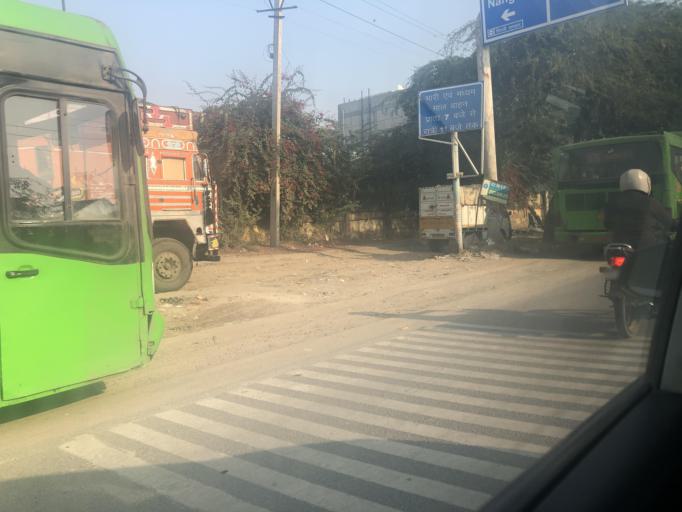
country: IN
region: Haryana
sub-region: Jhajjar
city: Bahadurgarh
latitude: 28.6195
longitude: 76.9739
